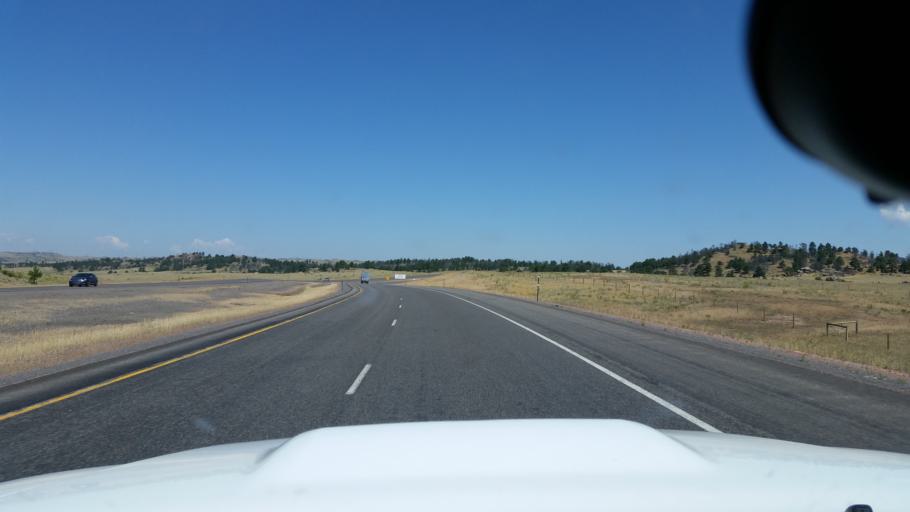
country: US
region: Wyoming
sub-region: Albany County
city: Laramie
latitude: 41.0032
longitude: -105.4149
